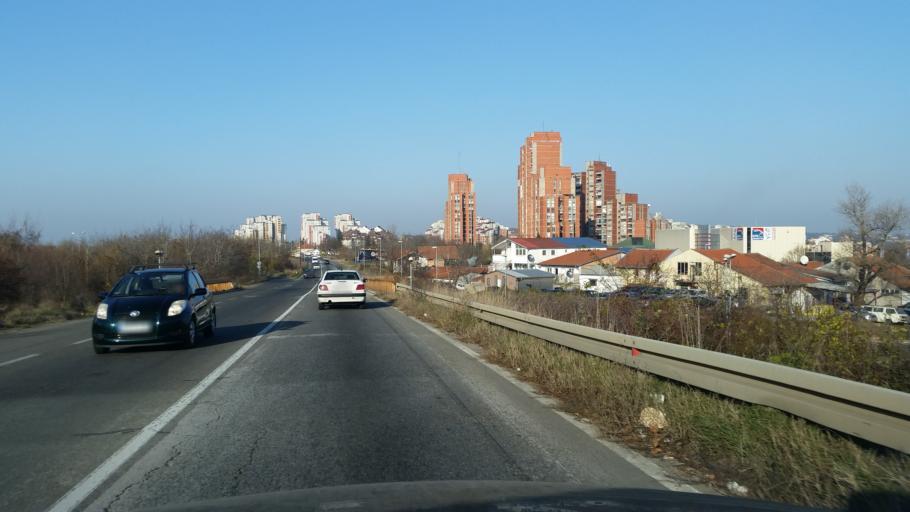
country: RS
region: Central Serbia
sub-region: Belgrade
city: Rakovica
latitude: 44.7299
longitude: 20.4201
